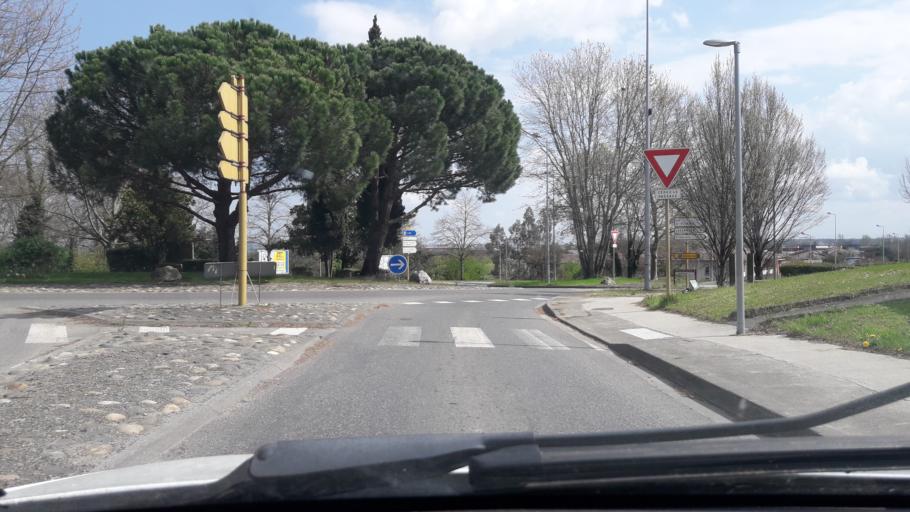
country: FR
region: Midi-Pyrenees
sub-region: Departement de la Haute-Garonne
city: Seysses
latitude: 43.4938
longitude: 1.3124
